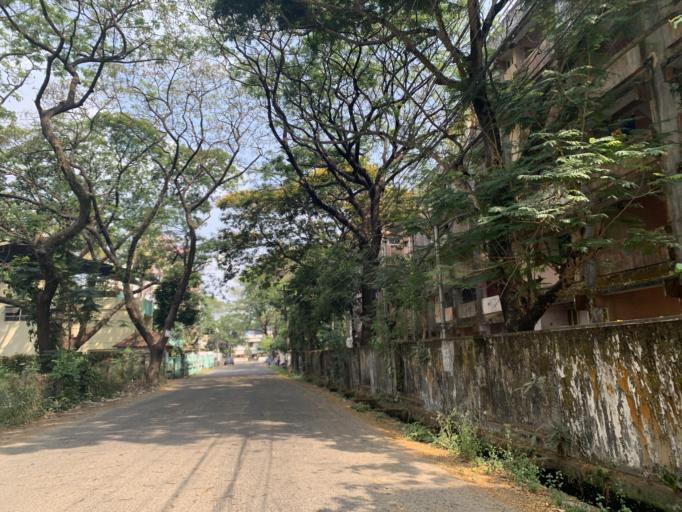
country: IN
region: Kerala
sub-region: Ernakulam
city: Cochin
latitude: 9.9578
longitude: 76.2979
